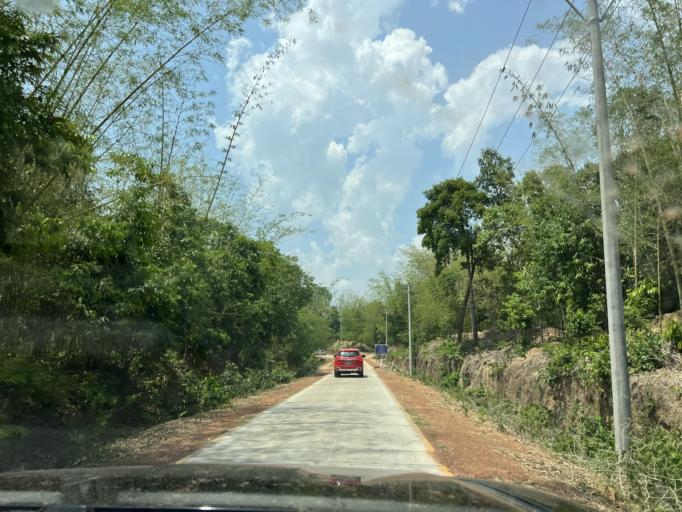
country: MM
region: Yangon
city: Twante
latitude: 16.6043
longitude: 95.9389
